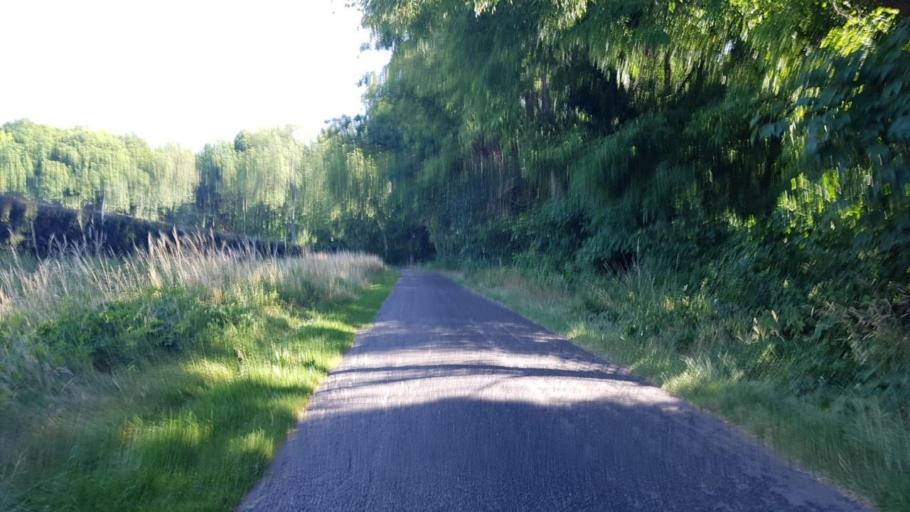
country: FR
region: Picardie
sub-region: Departement de l'Oise
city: Pontpoint
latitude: 49.2937
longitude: 2.6459
